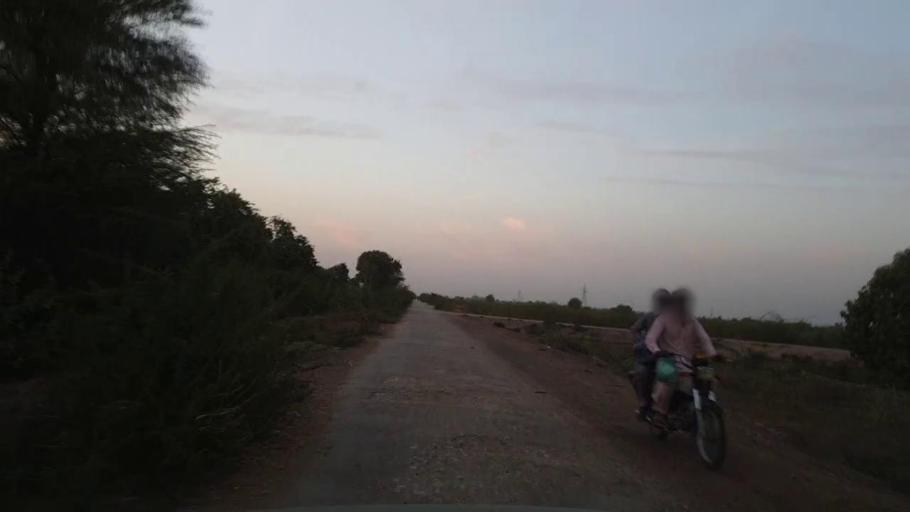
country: PK
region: Sindh
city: Kunri
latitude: 25.1477
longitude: 69.5567
